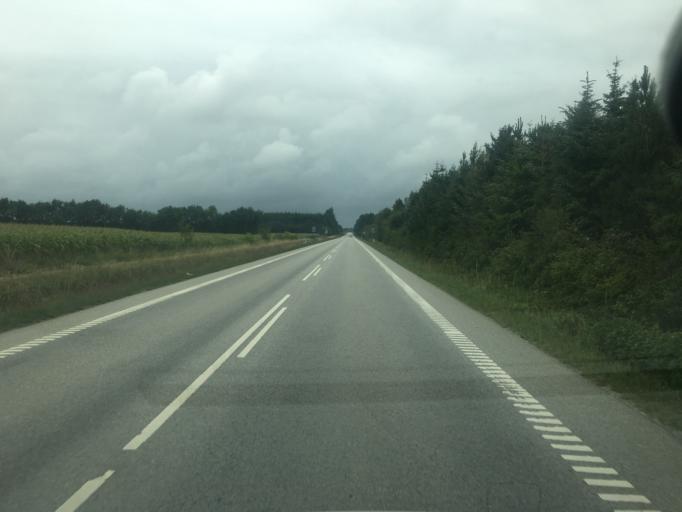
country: DK
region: South Denmark
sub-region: Haderslev Kommune
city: Vojens
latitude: 55.2208
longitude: 9.3014
